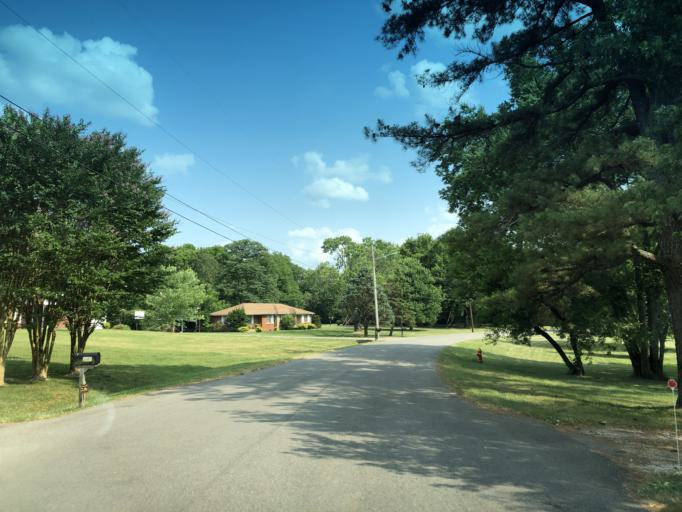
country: US
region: Tennessee
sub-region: Davidson County
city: Goodlettsville
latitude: 36.2604
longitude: -86.7238
